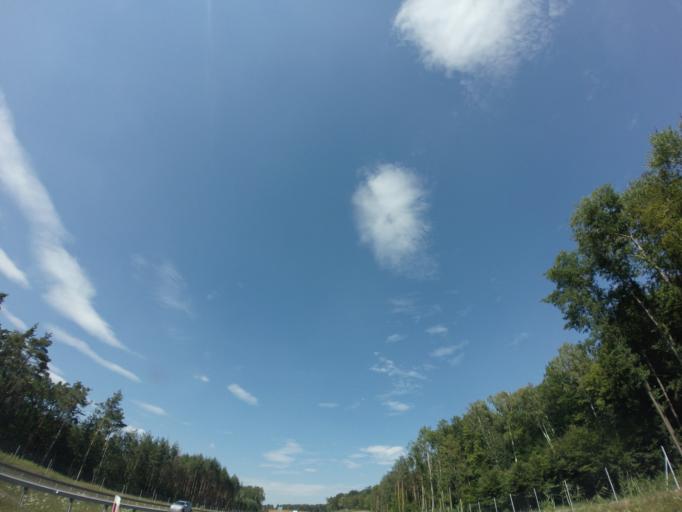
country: PL
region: Lower Silesian Voivodeship
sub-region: Legnica
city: Legnica
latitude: 51.2912
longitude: 16.1550
